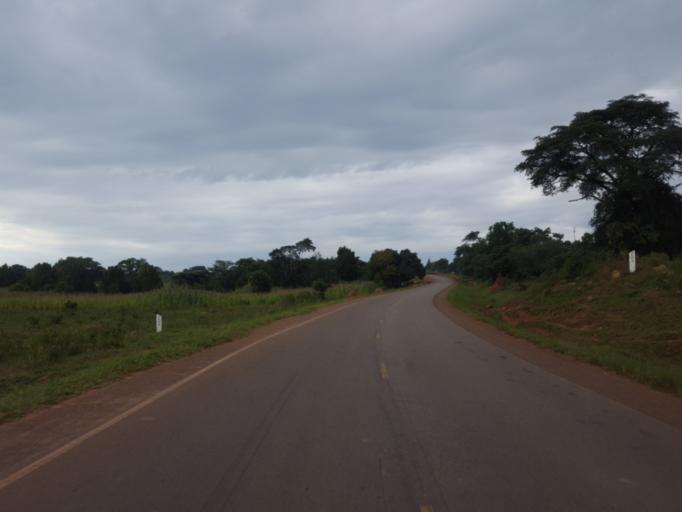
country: UG
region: Central Region
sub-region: Kiboga District
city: Kiboga
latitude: 1.0175
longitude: 31.6892
